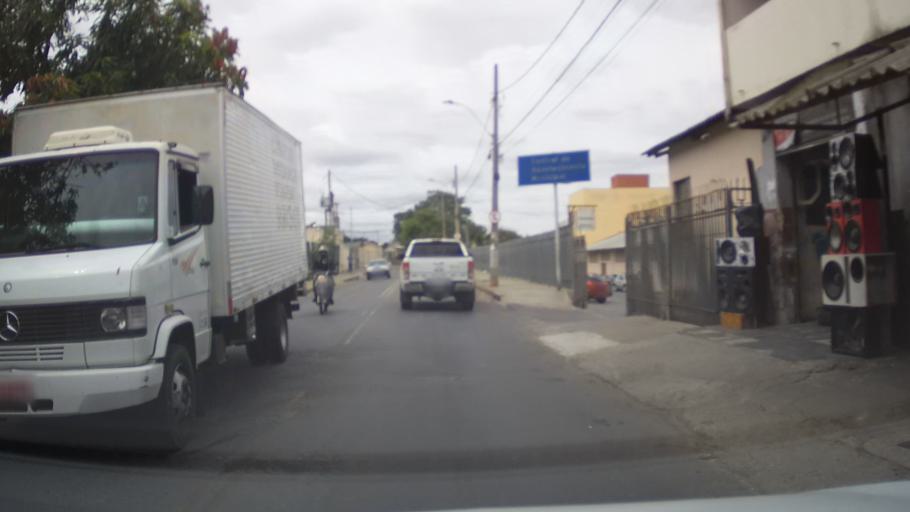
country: BR
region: Minas Gerais
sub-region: Belo Horizonte
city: Belo Horizonte
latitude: -19.8655
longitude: -43.9255
